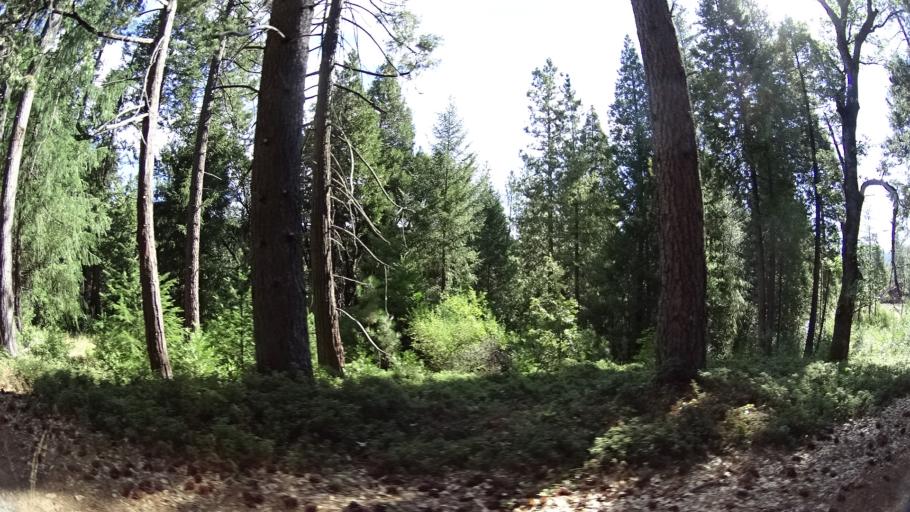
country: US
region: California
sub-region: Amador County
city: Pioneer
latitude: 38.3867
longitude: -120.4519
